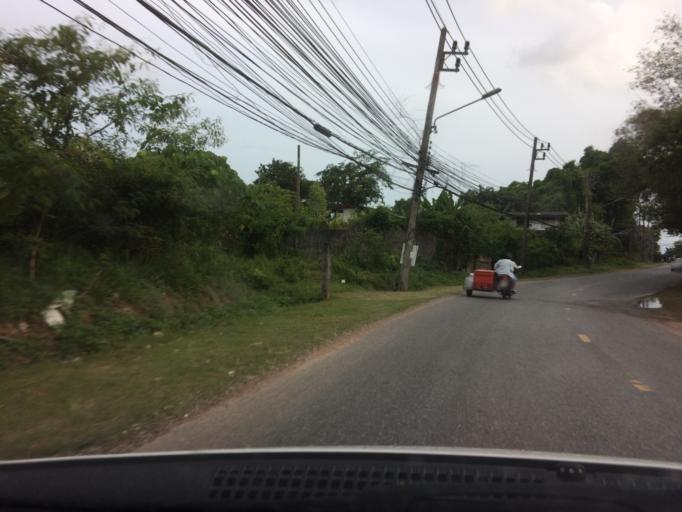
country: TH
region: Phuket
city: Phuket
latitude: 7.8910
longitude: 98.4069
